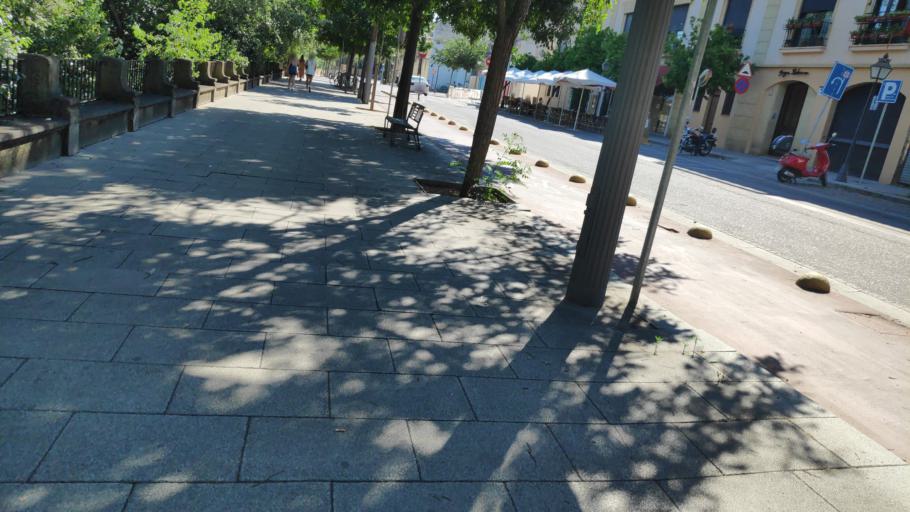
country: ES
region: Andalusia
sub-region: Province of Cordoba
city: Cordoba
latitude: 37.8785
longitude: -4.7773
